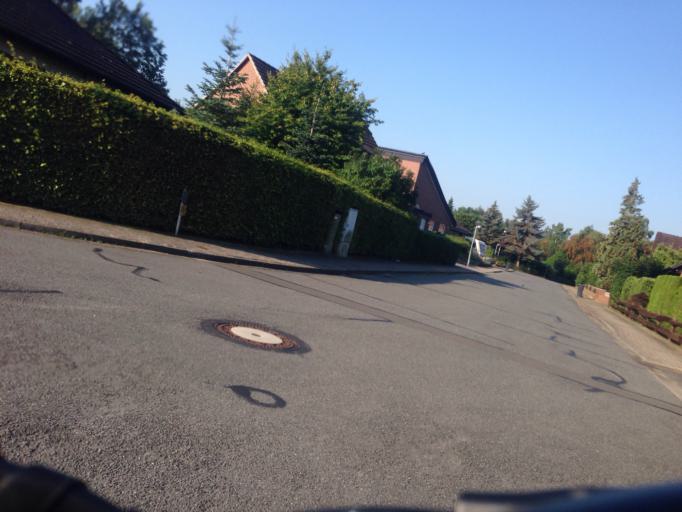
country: DE
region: Lower Saxony
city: Adendorf
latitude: 53.2842
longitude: 10.4299
